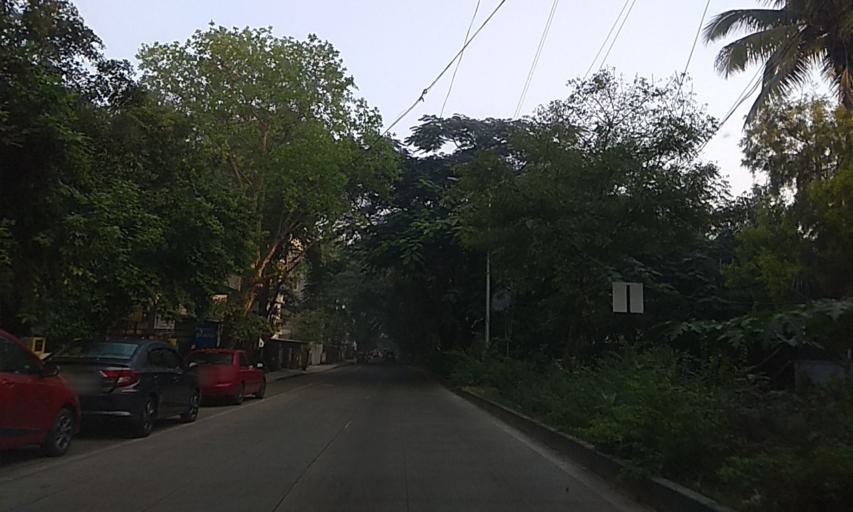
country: IN
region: Maharashtra
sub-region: Pune Division
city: Shivaji Nagar
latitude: 18.5437
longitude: 73.8172
